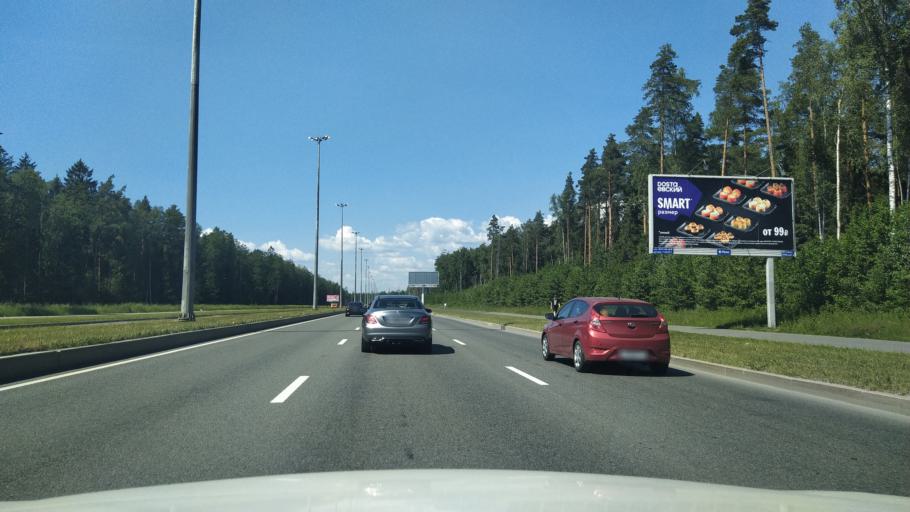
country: RU
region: Leningrad
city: Untolovo
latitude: 60.0552
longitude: 30.2244
